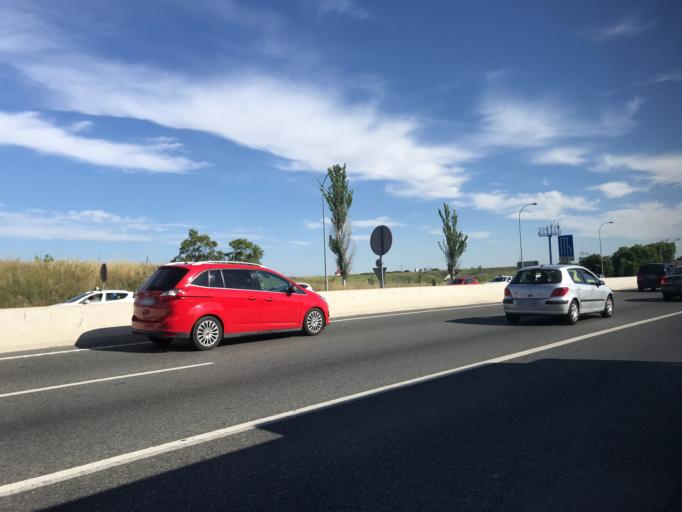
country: ES
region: Madrid
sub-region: Provincia de Madrid
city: San Blas
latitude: 40.4334
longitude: -3.5952
